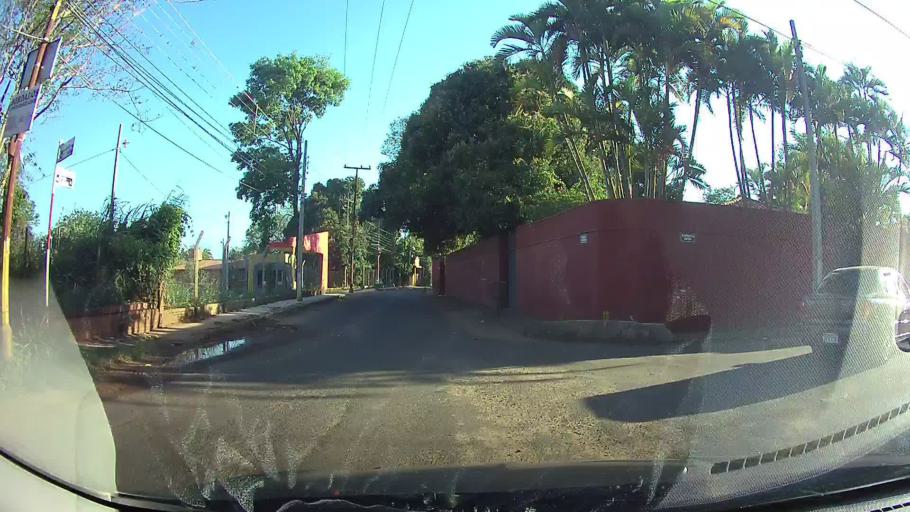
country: PY
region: Central
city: Fernando de la Mora
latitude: -25.3436
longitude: -57.5326
